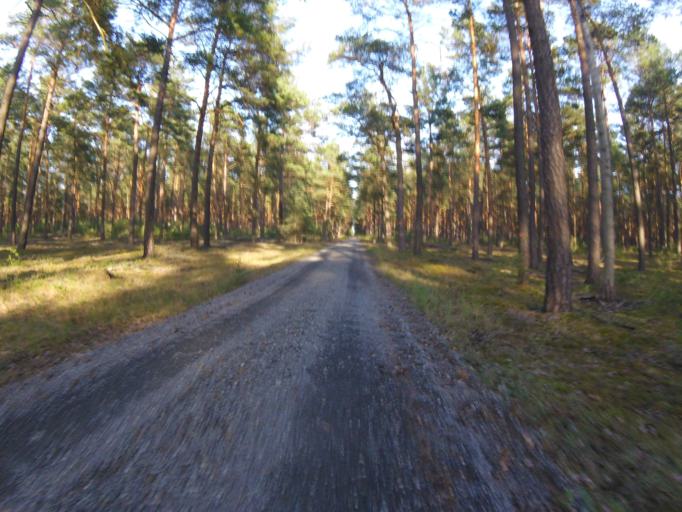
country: DE
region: Brandenburg
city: Gross Koris
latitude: 52.1785
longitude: 13.7159
